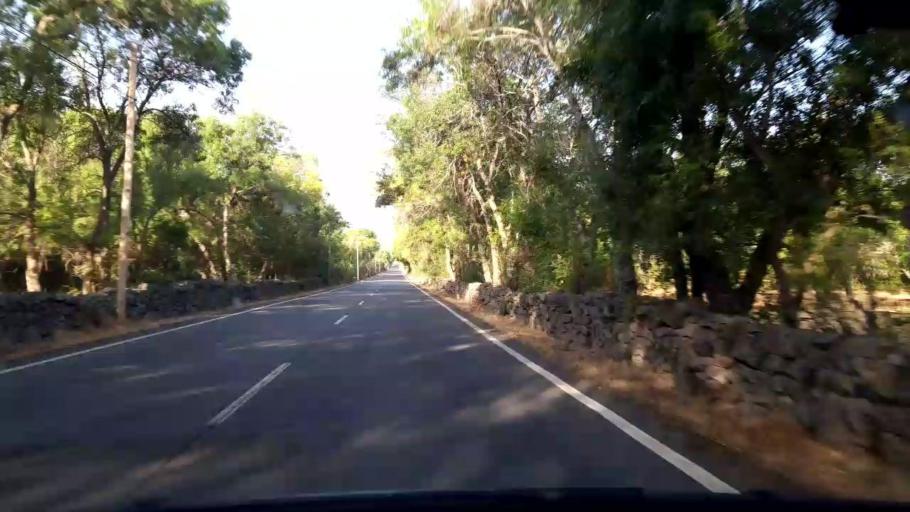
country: ES
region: Madrid
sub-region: Provincia de Madrid
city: Guadarrama
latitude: 40.6812
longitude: -4.0699
